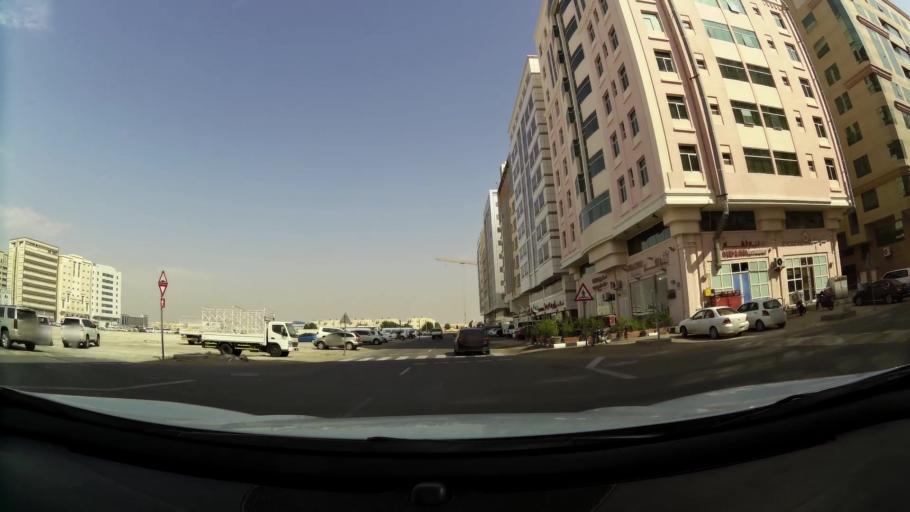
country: AE
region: Abu Dhabi
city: Abu Dhabi
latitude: 24.3417
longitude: 54.5351
